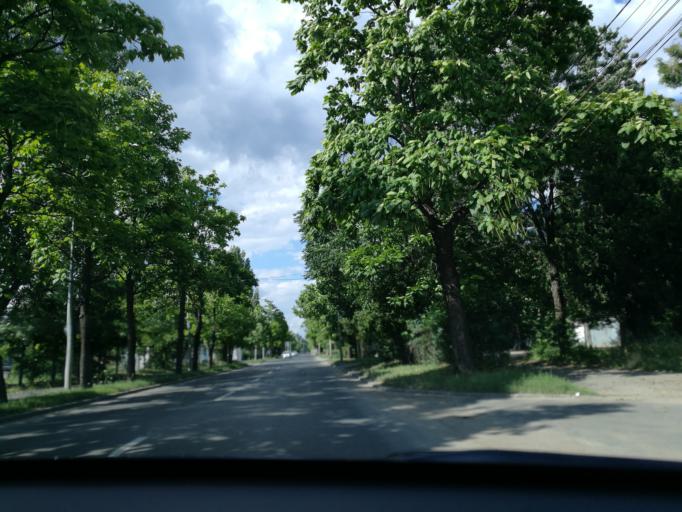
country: RO
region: Ilfov
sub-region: Comuna Glina
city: Catelu
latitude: 44.4186
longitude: 26.2182
